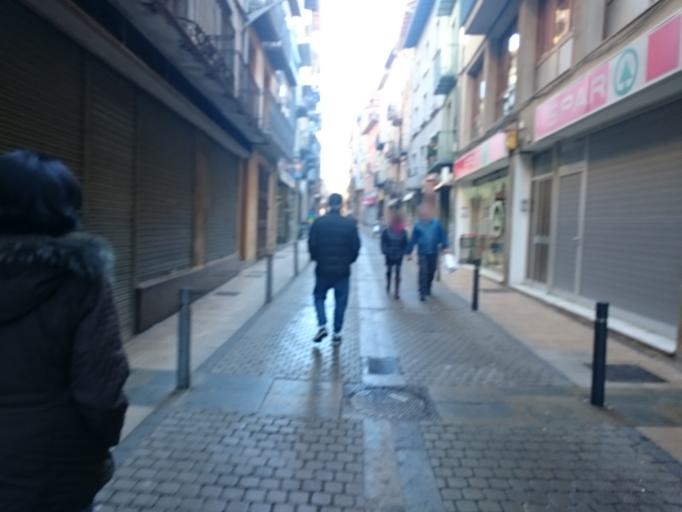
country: ES
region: Catalonia
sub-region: Provincia de Girona
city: Camprodon
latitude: 42.3137
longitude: 2.3657
